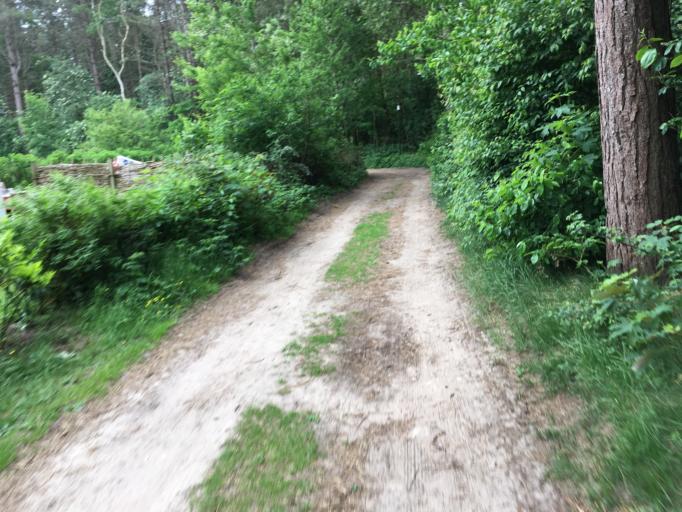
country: DE
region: Schleswig-Holstein
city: Norddorf
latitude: 54.6738
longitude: 8.3313
